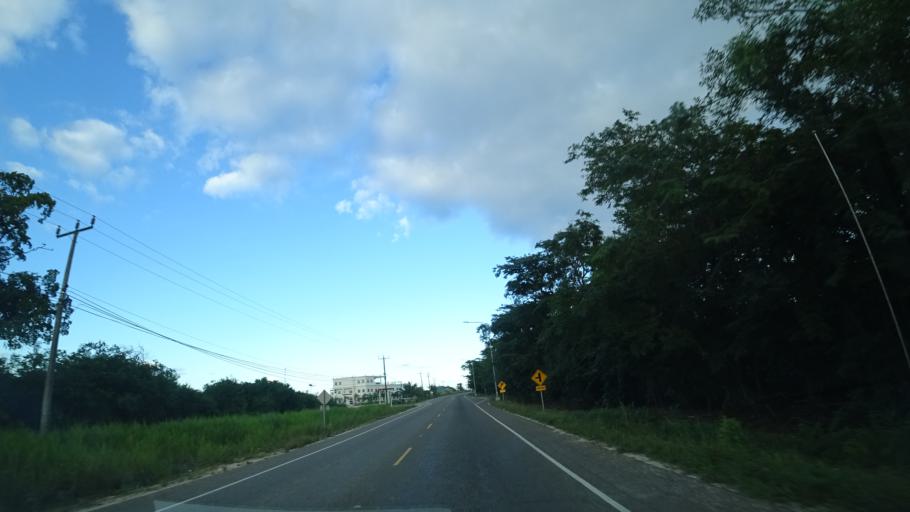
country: BZ
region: Belize
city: Belize City
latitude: 17.5435
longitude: -88.2602
